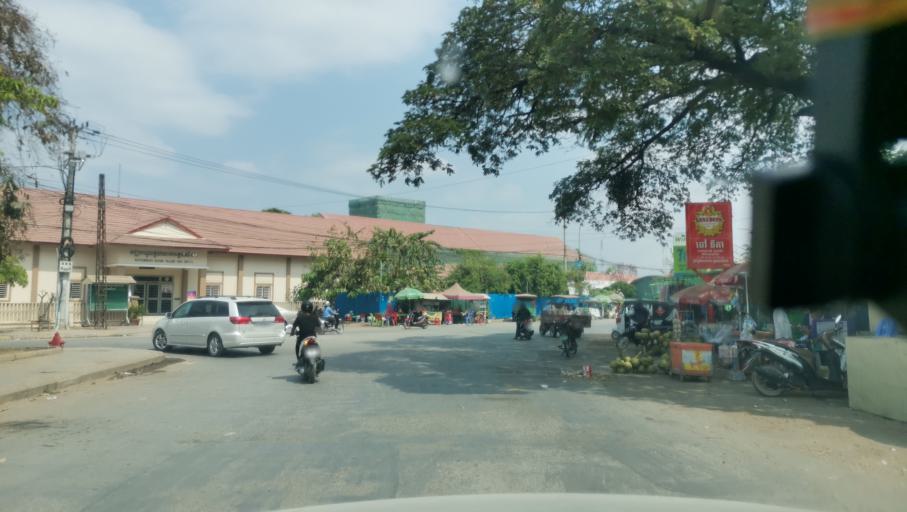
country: KH
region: Battambang
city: Battambang
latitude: 13.1070
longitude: 103.2012
